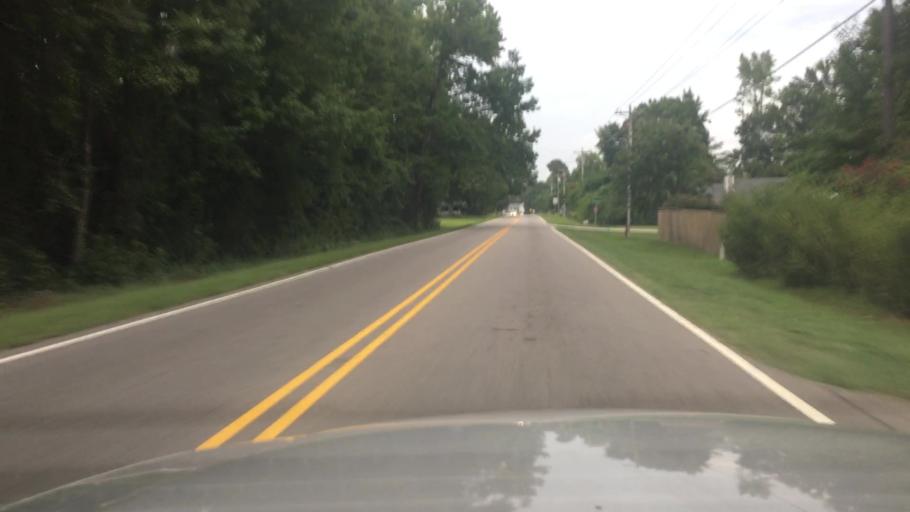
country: US
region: North Carolina
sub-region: Hoke County
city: Rockfish
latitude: 34.9623
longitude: -79.0530
